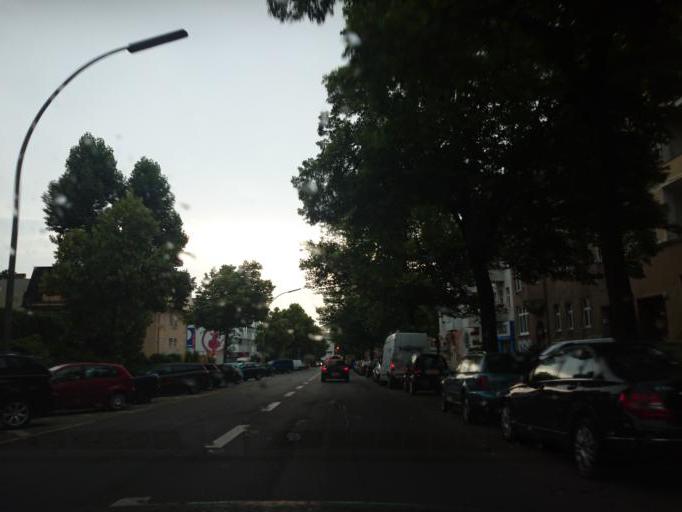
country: DE
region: Berlin
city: Mariendorf
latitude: 52.4561
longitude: 13.3786
